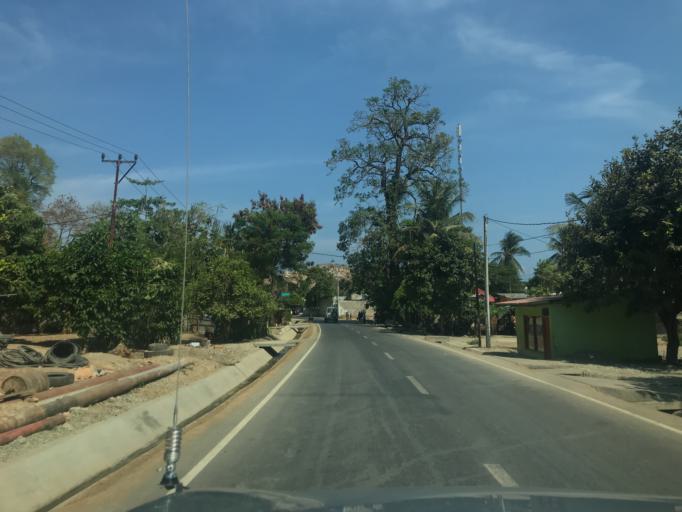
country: TL
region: Dili
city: Dili
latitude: -8.5557
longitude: 125.5188
